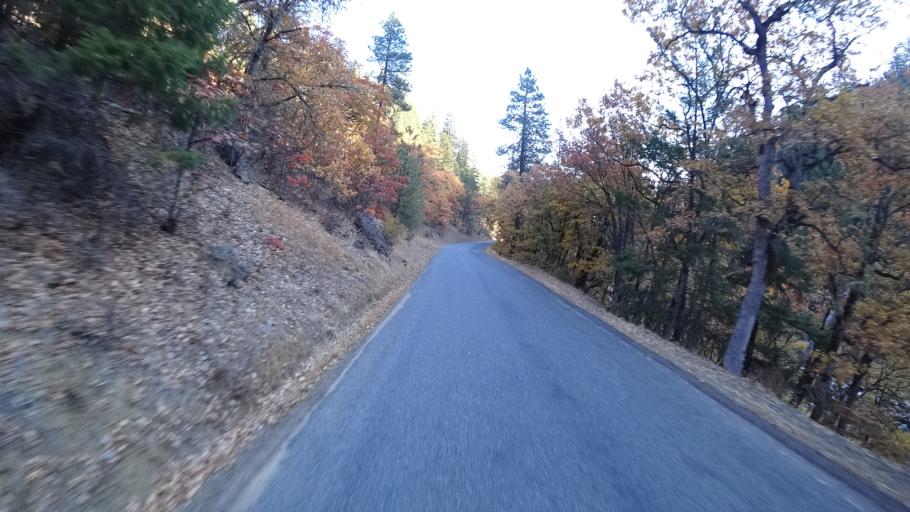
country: US
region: California
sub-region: Siskiyou County
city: Happy Camp
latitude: 41.6384
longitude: -123.0656
